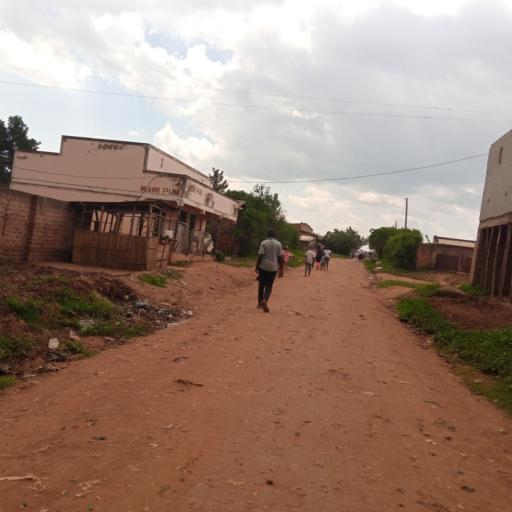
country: UG
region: Eastern Region
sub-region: Mbale District
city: Mbale
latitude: 1.0962
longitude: 34.1774
